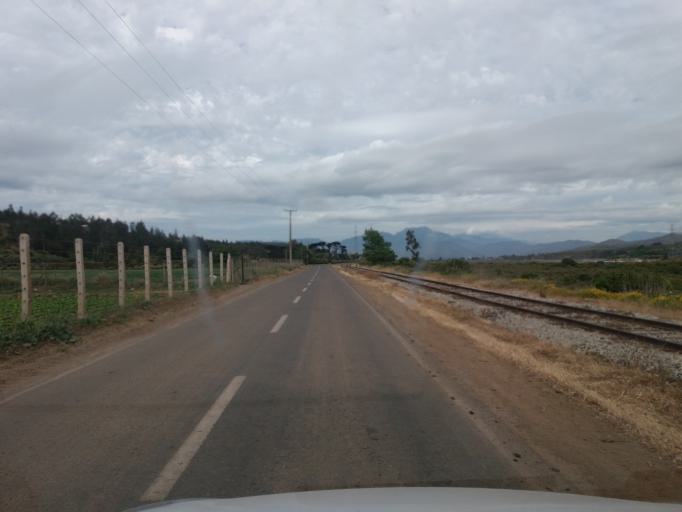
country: CL
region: Valparaiso
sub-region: Provincia de Marga Marga
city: Villa Alemana
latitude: -32.9166
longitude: -71.4100
